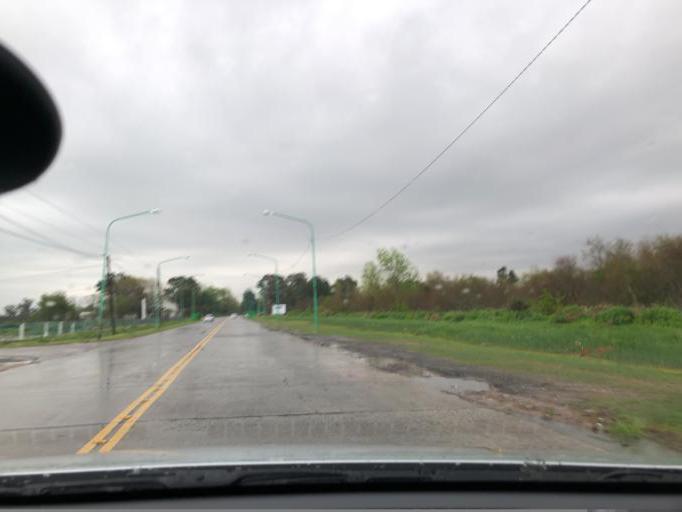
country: AR
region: Buenos Aires
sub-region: Partido de Ensenada
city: Ensenada
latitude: -34.8460
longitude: -57.9305
